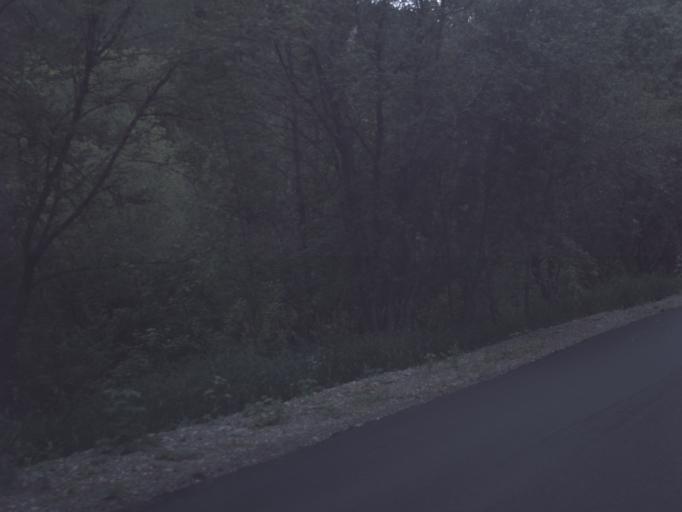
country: US
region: Utah
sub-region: Utah County
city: Cedar Hills
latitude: 40.4475
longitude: -111.6429
